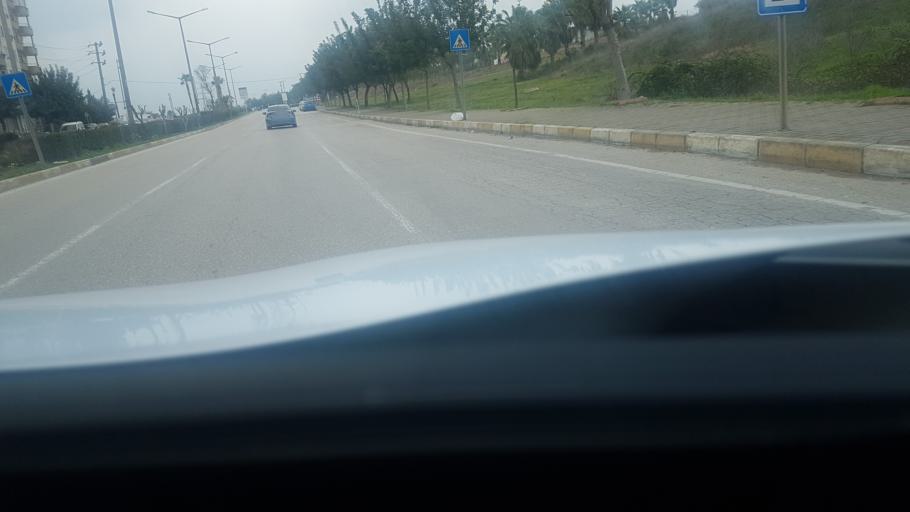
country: TR
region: Adana
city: Seyhan
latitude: 37.0545
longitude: 35.2498
